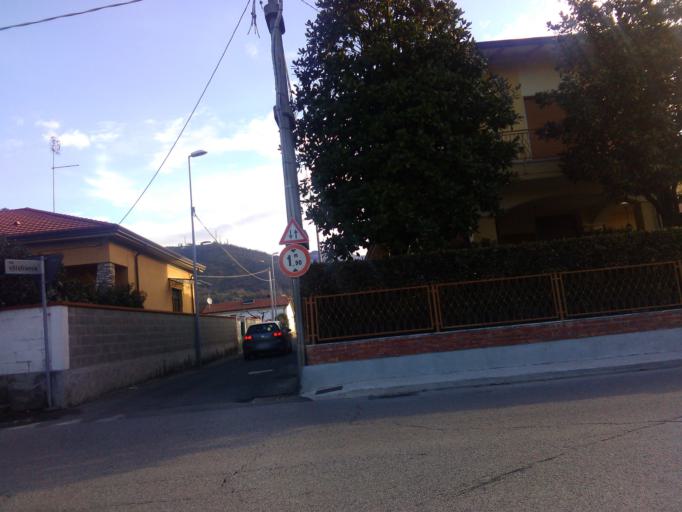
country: IT
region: Tuscany
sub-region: Provincia di Massa-Carrara
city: Carrara
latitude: 44.0550
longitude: 10.0517
